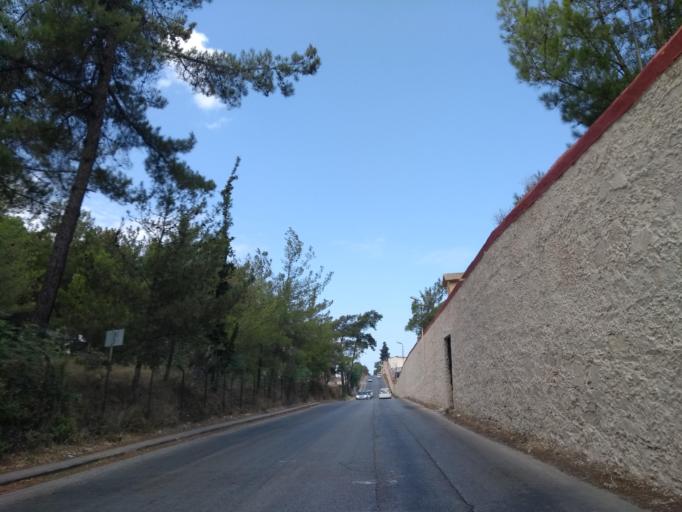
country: GR
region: Crete
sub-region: Nomos Chanias
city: Souda
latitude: 35.4856
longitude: 24.0845
